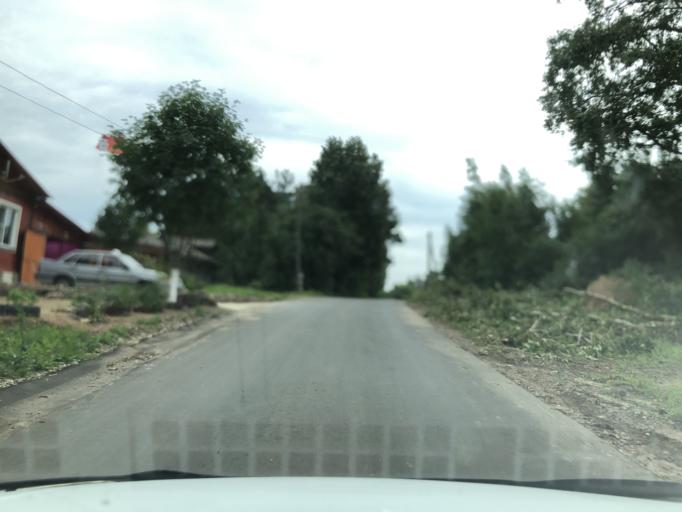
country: RU
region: Jaroslavl
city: Petrovsk
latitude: 57.0069
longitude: 39.2583
